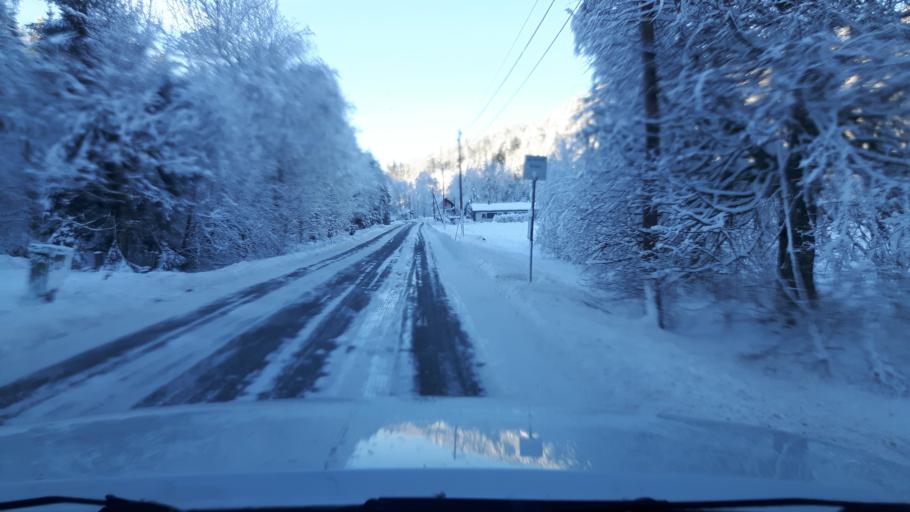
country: SE
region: Halland
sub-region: Kungsbacka Kommun
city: Fjaeras kyrkby
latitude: 57.5527
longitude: 12.1976
